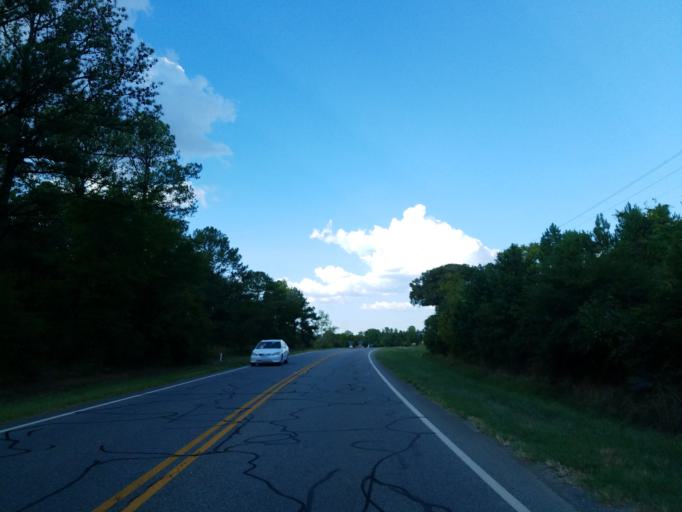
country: US
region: Georgia
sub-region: Bartow County
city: Rydal
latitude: 34.5152
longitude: -84.7100
